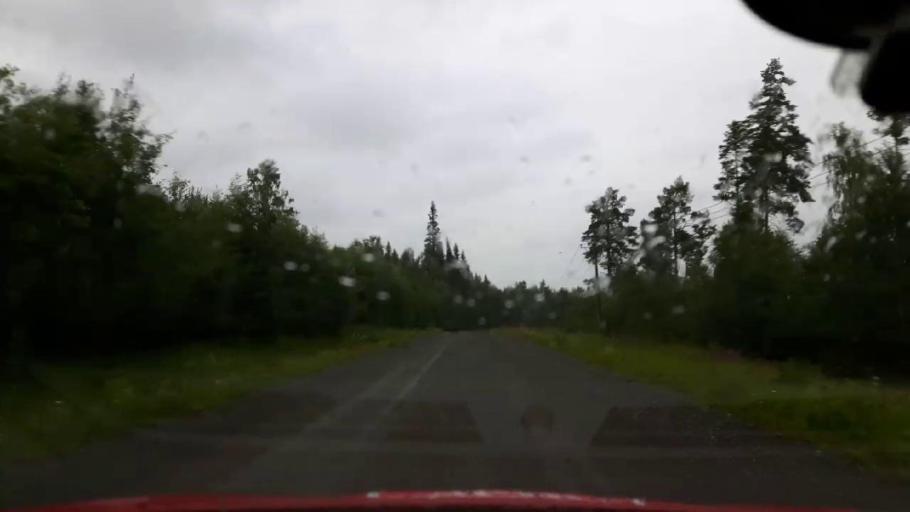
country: SE
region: Jaemtland
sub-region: OEstersunds Kommun
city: Brunflo
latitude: 62.8552
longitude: 14.9466
